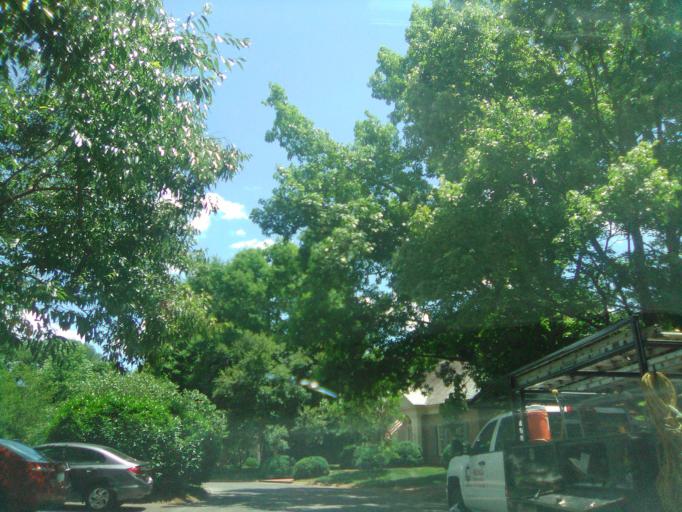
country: US
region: Tennessee
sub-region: Davidson County
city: Belle Meade
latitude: 36.1160
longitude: -86.8570
